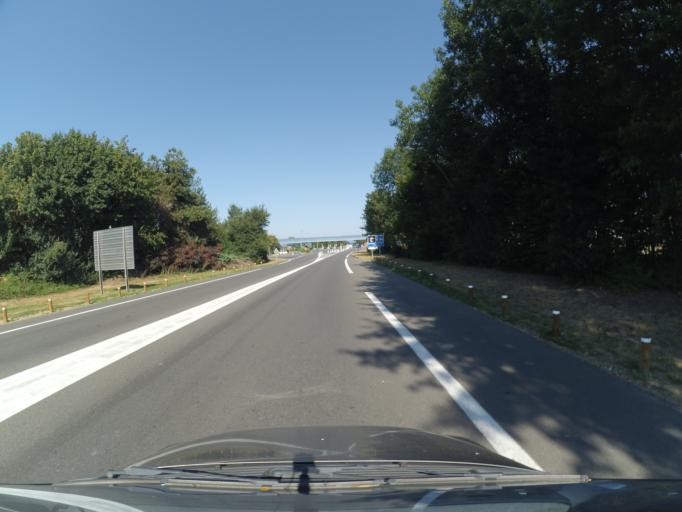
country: FR
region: Pays de la Loire
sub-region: Departement de la Vendee
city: Bouffere
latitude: 46.9584
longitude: -1.3504
